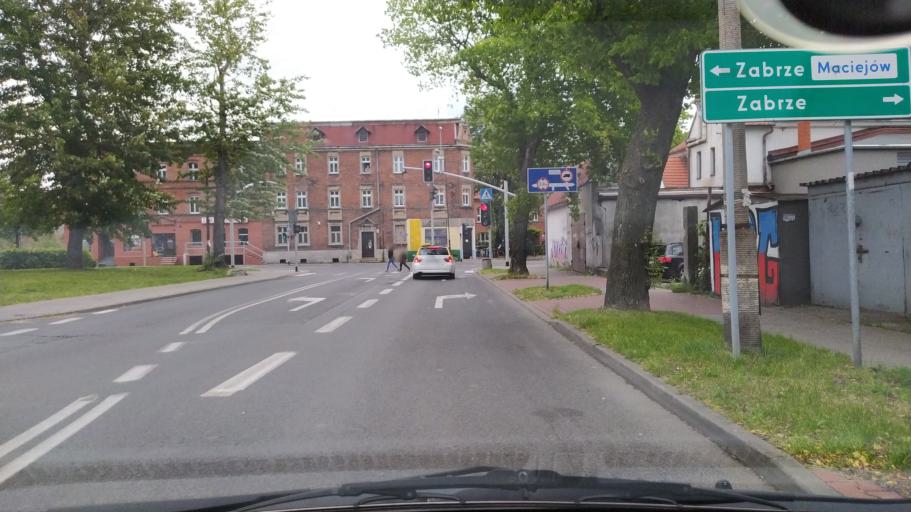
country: PL
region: Silesian Voivodeship
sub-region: Powiat gliwicki
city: Przyszowice
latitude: 50.2932
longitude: 18.7312
